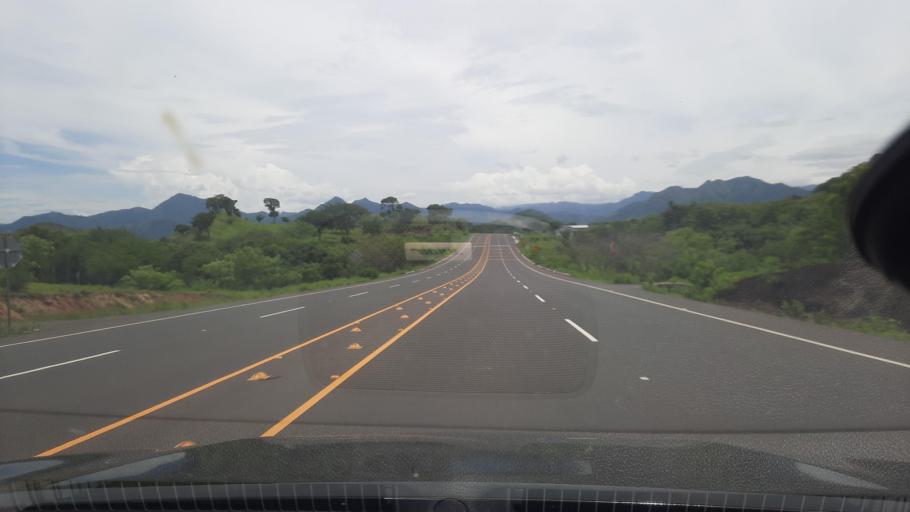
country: HN
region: Valle
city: Aramecina
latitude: 13.7905
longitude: -87.7013
